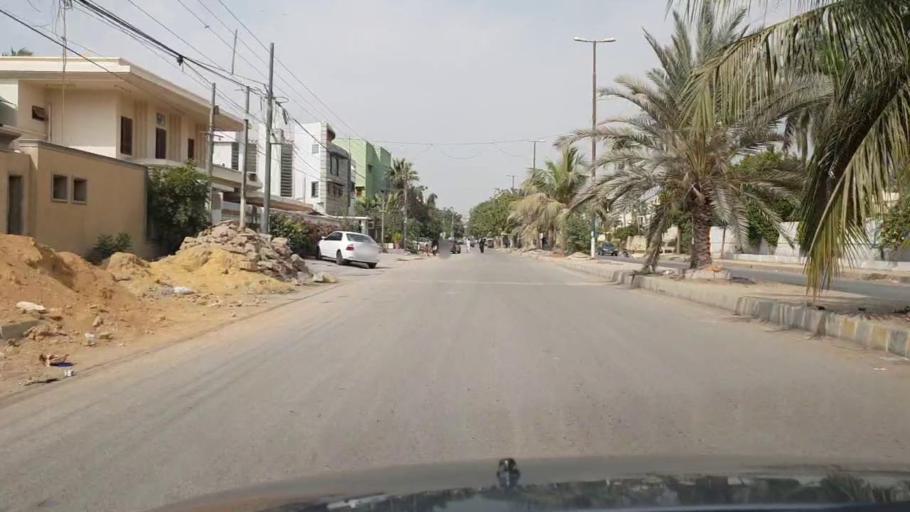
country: PK
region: Sindh
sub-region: Karachi District
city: Karachi
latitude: 24.8737
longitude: 67.0869
